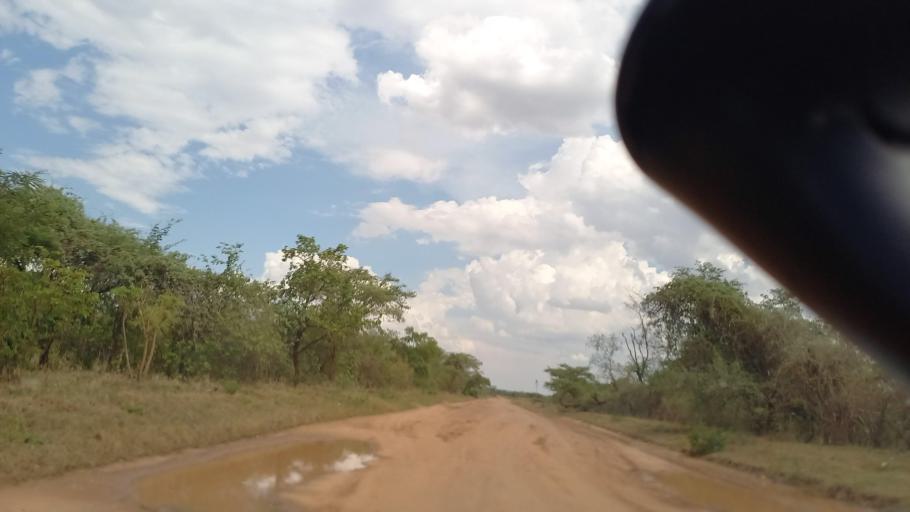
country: ZM
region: Southern
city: Nakambala
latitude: -16.0521
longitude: 27.9852
